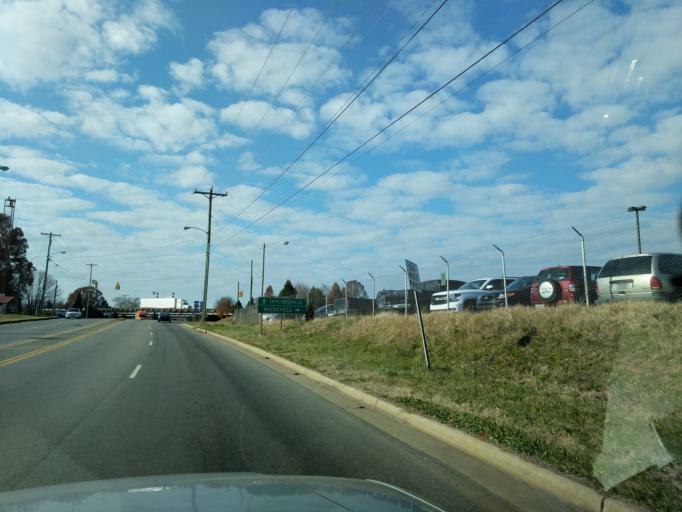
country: US
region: North Carolina
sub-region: Iredell County
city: Statesville
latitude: 35.7930
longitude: -80.9335
